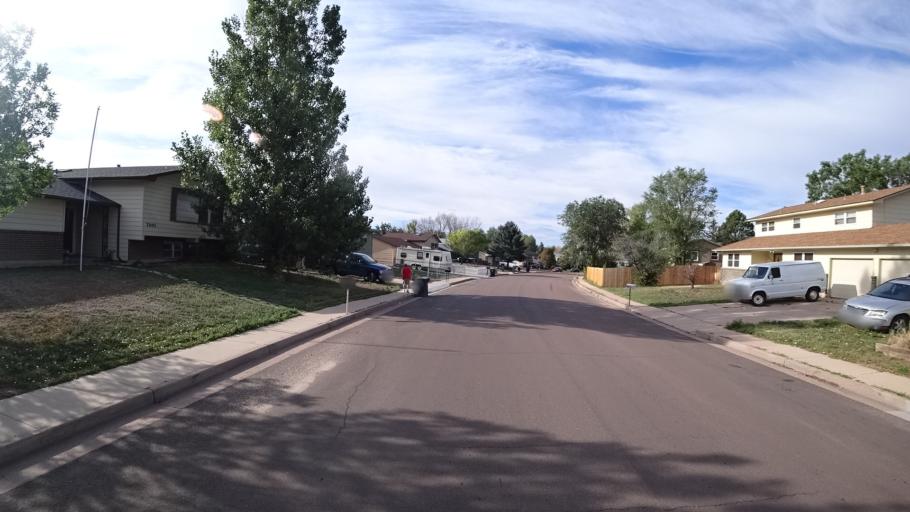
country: US
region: Colorado
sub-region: El Paso County
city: Security-Widefield
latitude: 38.7303
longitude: -104.6923
